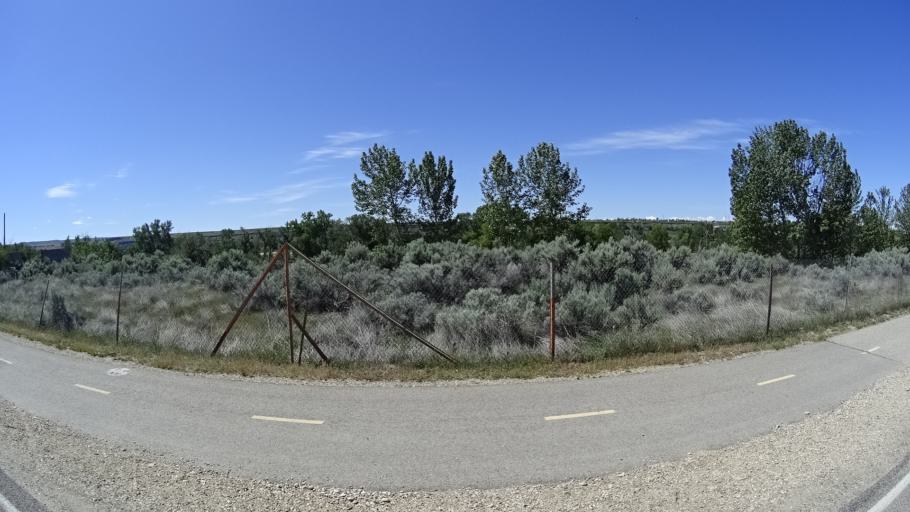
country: US
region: Idaho
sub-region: Ada County
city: Boise
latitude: 43.5625
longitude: -116.1066
